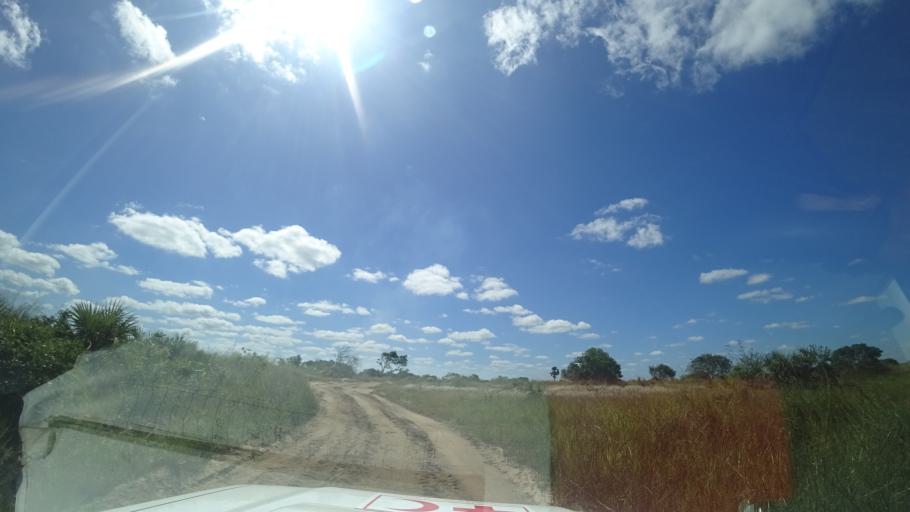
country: MZ
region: Sofala
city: Dondo
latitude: -19.4562
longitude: 34.5947
